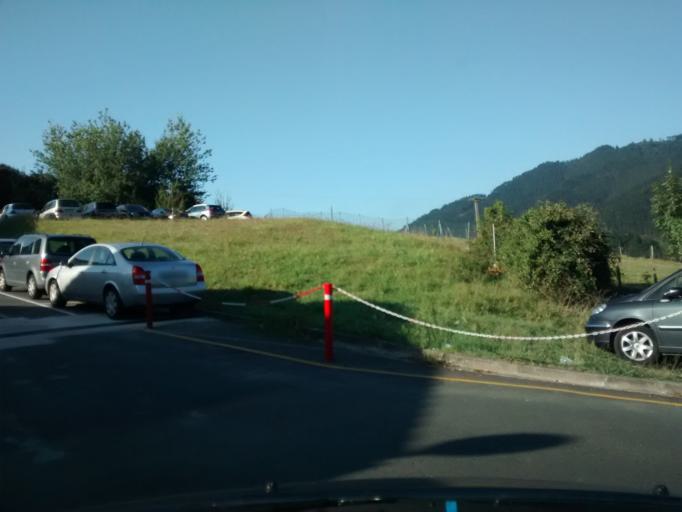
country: ES
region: Basque Country
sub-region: Provincia de Guipuzcoa
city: Mendaro
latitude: 43.2507
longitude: -2.3860
